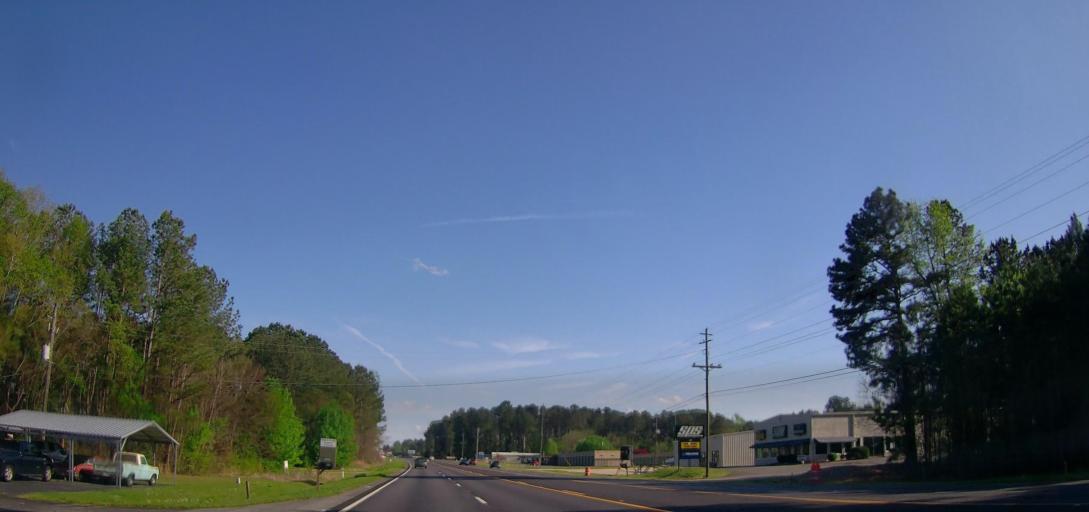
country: US
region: Georgia
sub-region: Baldwin County
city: Milledgeville
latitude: 33.1815
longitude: -83.2889
